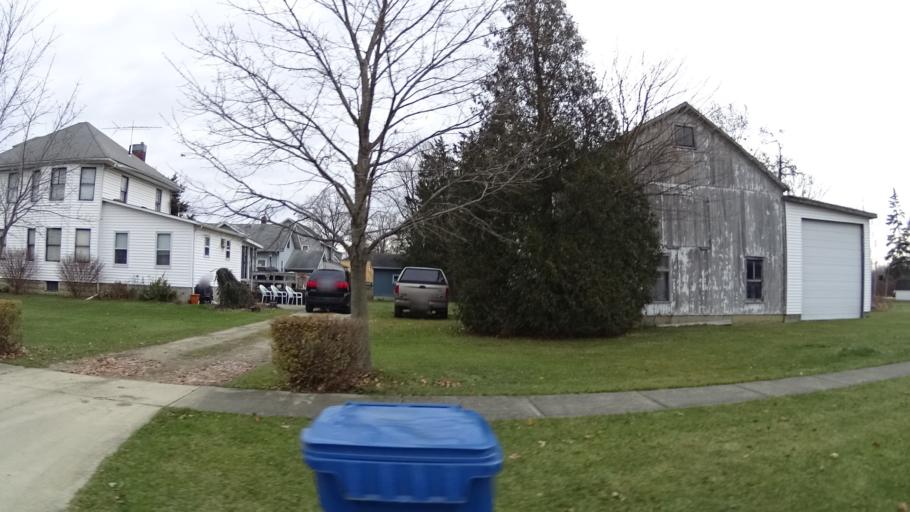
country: US
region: Ohio
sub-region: Lorain County
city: Wellington
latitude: 41.1681
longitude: -82.2102
